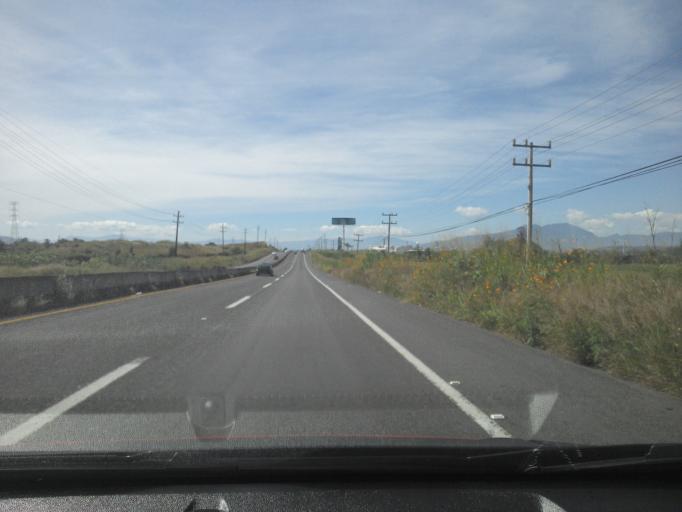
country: MX
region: Jalisco
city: Tala
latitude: 20.6755
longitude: -103.7054
